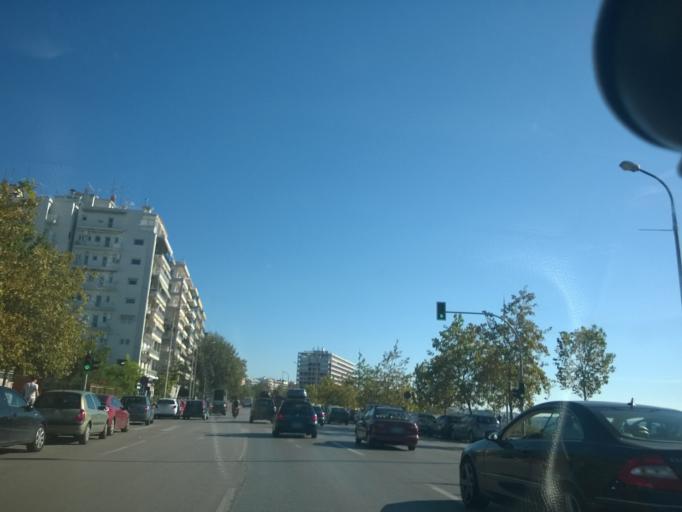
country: GR
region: Central Macedonia
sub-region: Nomos Thessalonikis
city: Agios Pavlos
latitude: 40.6220
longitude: 22.9520
